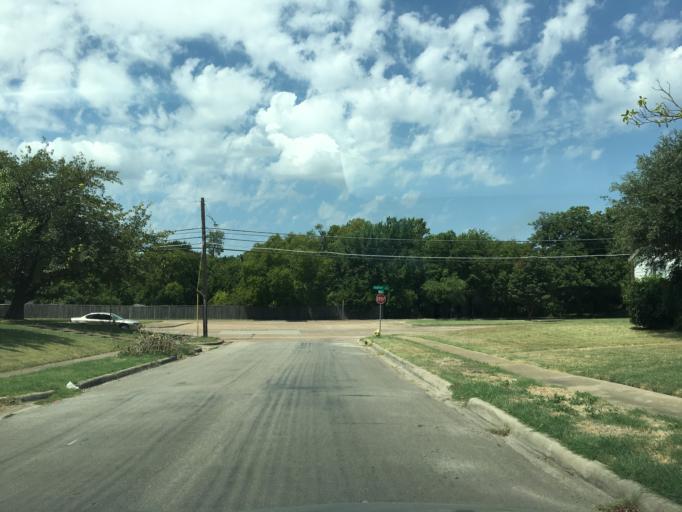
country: US
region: Texas
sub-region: Dallas County
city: Garland
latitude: 32.8591
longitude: -96.6824
